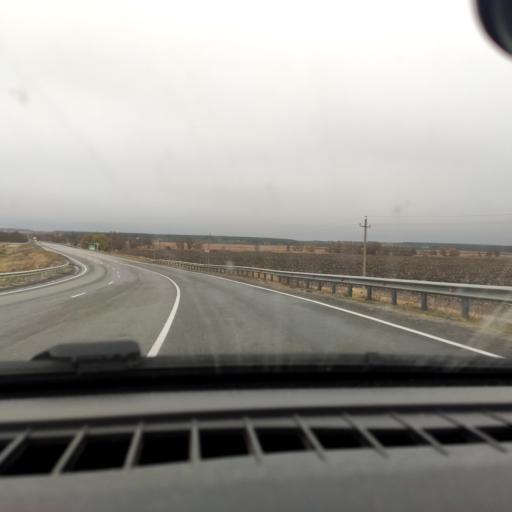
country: RU
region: Voronezj
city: Ostrogozhsk
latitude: 51.0270
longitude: 38.9874
